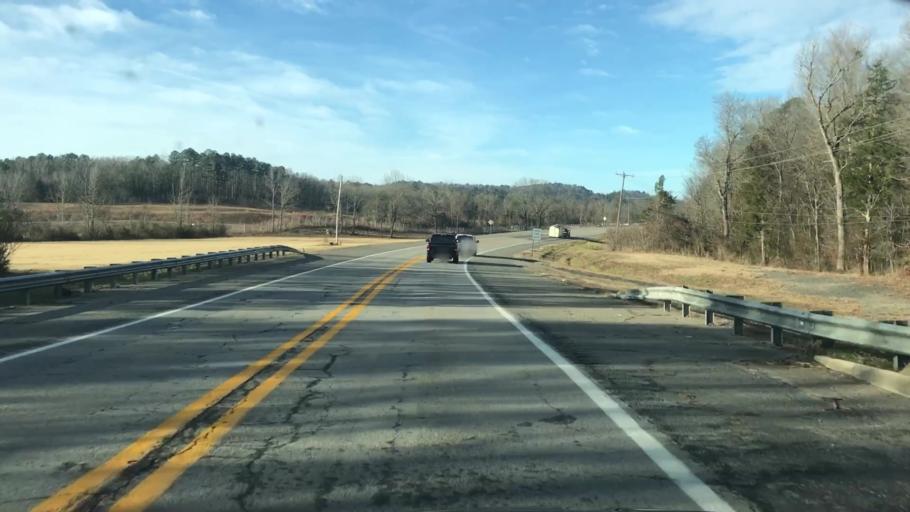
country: US
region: Arkansas
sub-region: Montgomery County
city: Mount Ida
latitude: 34.5321
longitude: -93.5210
